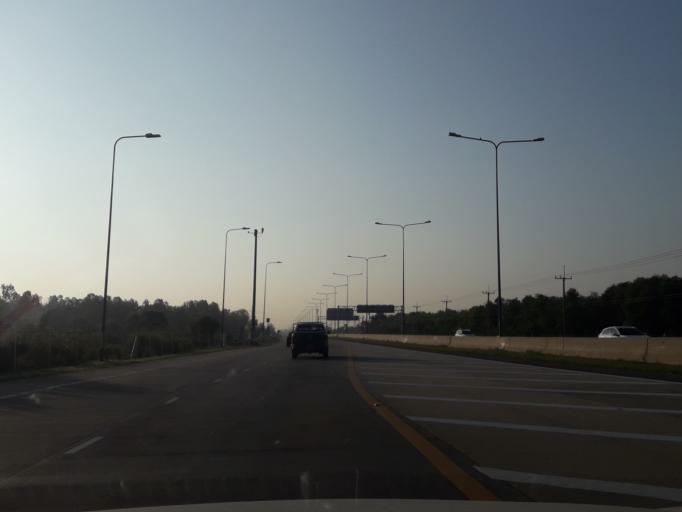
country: TH
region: Pathum Thani
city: Sam Khok
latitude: 14.1426
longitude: 100.5589
